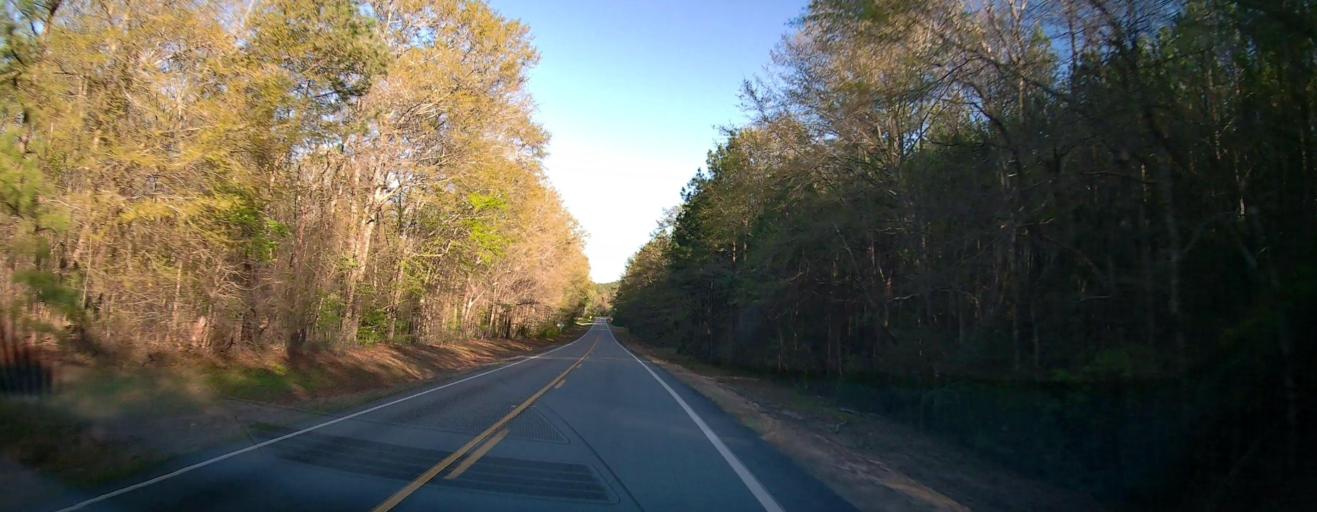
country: US
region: Georgia
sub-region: Wilkinson County
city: Irwinton
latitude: 32.9432
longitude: -83.1604
